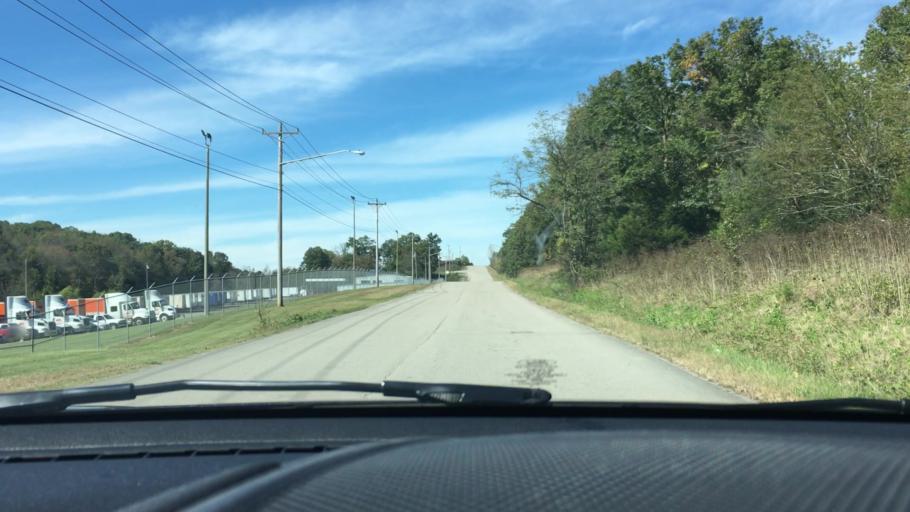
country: US
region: Tennessee
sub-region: Giles County
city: Pulaski
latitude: 35.2192
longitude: -87.0635
